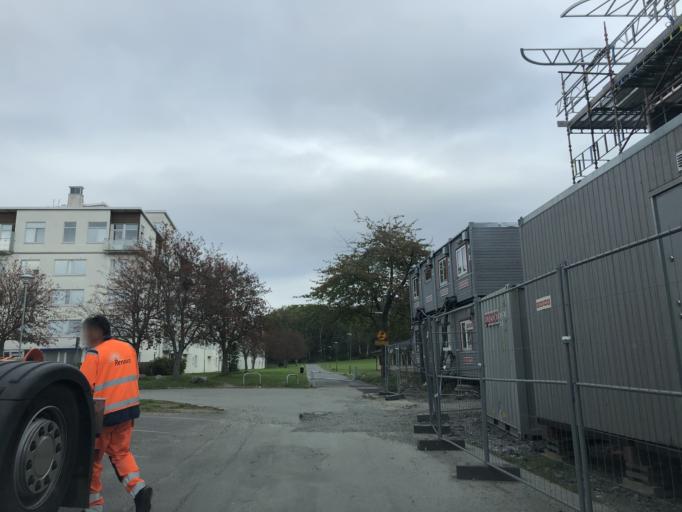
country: SE
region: Vaestra Goetaland
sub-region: Goteborg
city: Majorna
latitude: 57.6561
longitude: 11.9052
